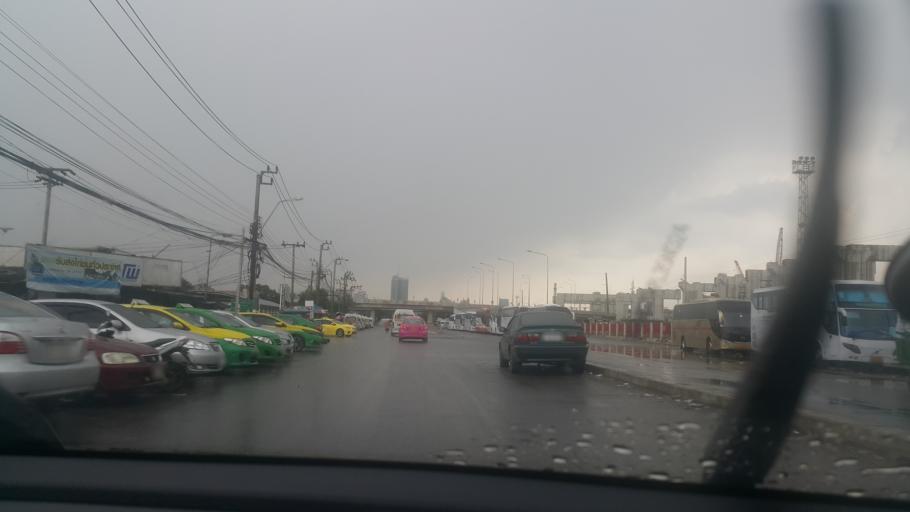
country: TH
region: Bangkok
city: Bang Sue
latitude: 13.8135
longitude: 100.5459
